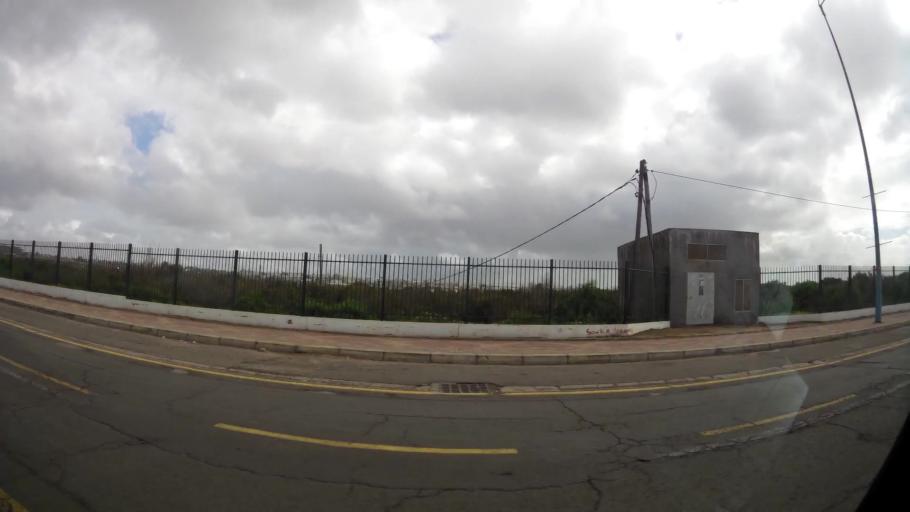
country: MA
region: Grand Casablanca
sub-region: Casablanca
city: Casablanca
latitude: 33.5826
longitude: -7.6949
